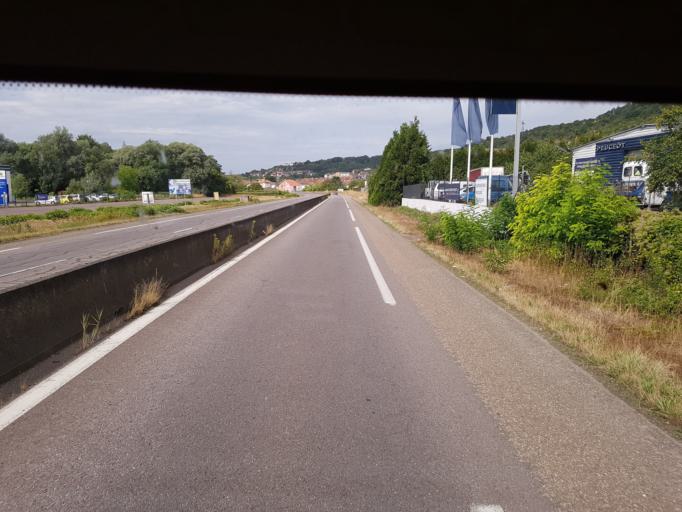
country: FR
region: Lorraine
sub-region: Departement de la Moselle
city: Rosselange
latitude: 49.2584
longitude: 6.0802
